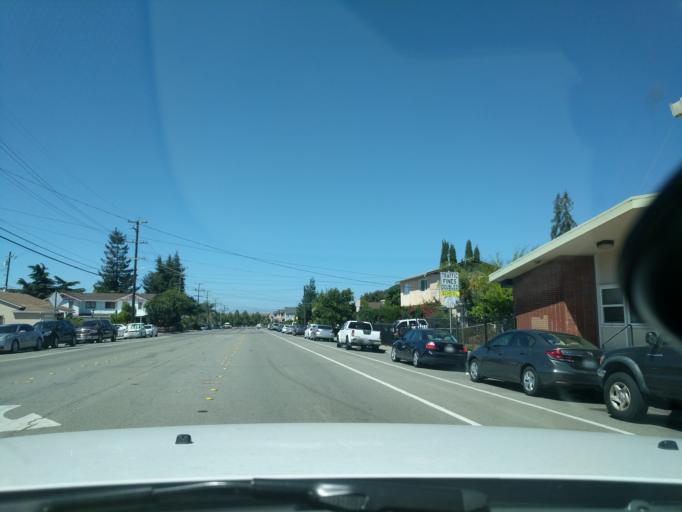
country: US
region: California
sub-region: Alameda County
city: Hayward
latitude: 37.6683
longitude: -122.0909
